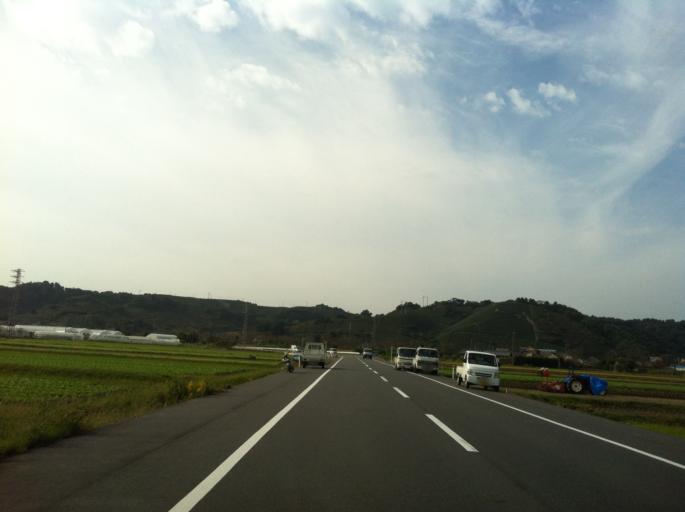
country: JP
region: Shizuoka
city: Sagara
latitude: 34.7521
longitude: 138.2069
